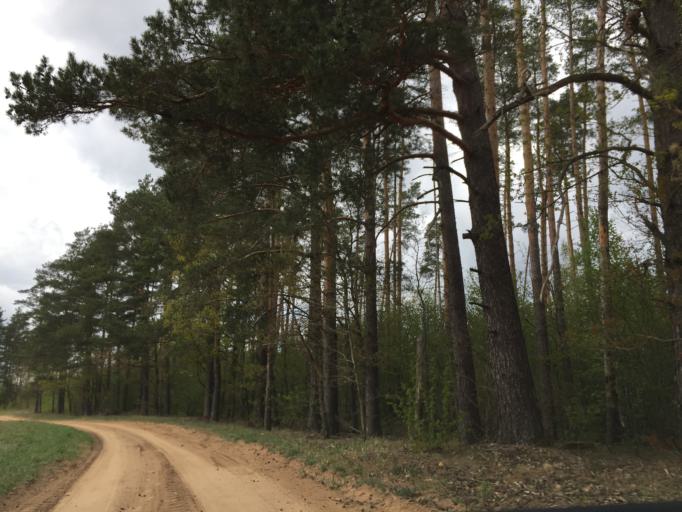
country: LV
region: Kekava
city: Kekava
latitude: 56.7999
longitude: 24.3056
